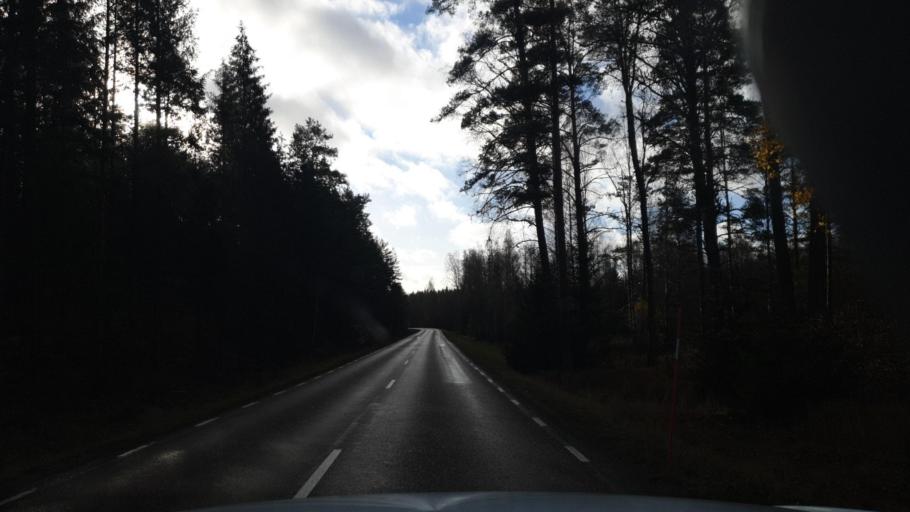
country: SE
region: Vaermland
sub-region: Grums Kommun
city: Grums
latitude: 59.4430
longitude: 12.9769
